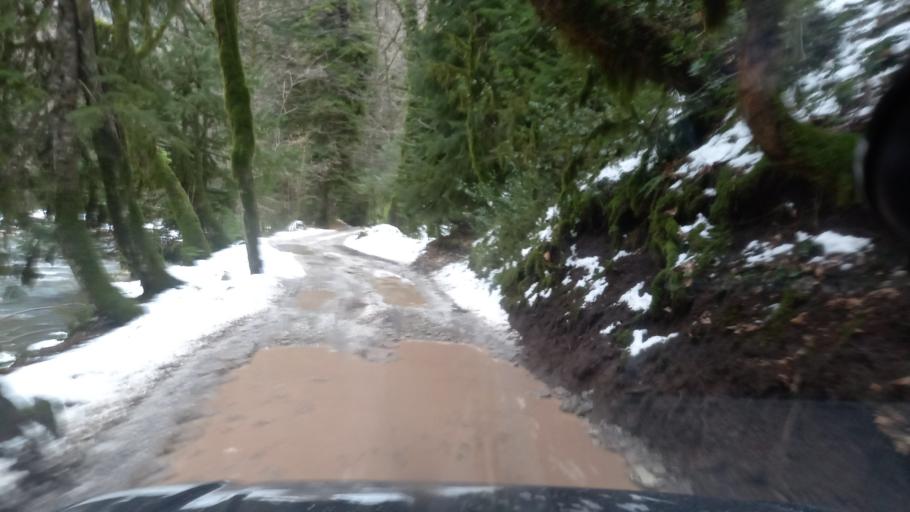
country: GE
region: Abkhazia
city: Gagra
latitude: 43.4331
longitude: 40.4445
